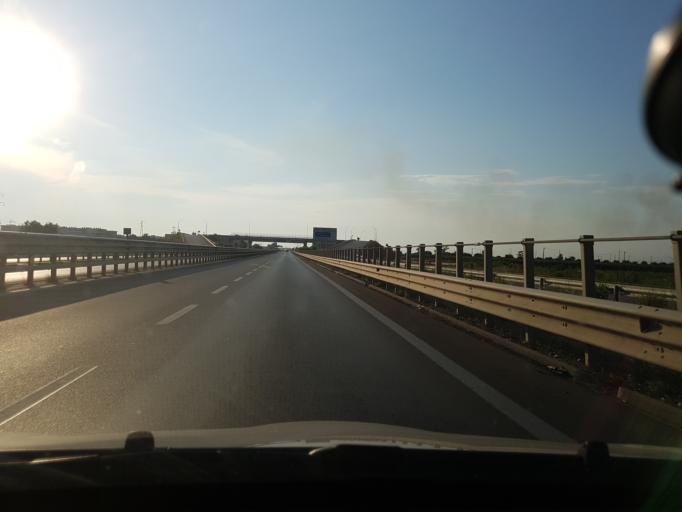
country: IT
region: Apulia
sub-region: Provincia di Foggia
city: Carapelle
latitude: 41.3611
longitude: 15.7075
